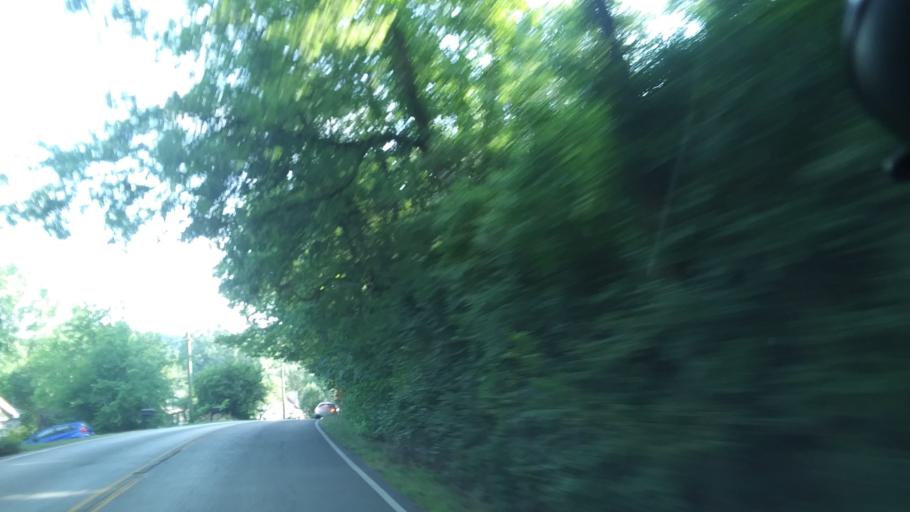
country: US
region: Tennessee
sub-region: Rutherford County
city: La Vergne
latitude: 36.0808
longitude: -86.6672
